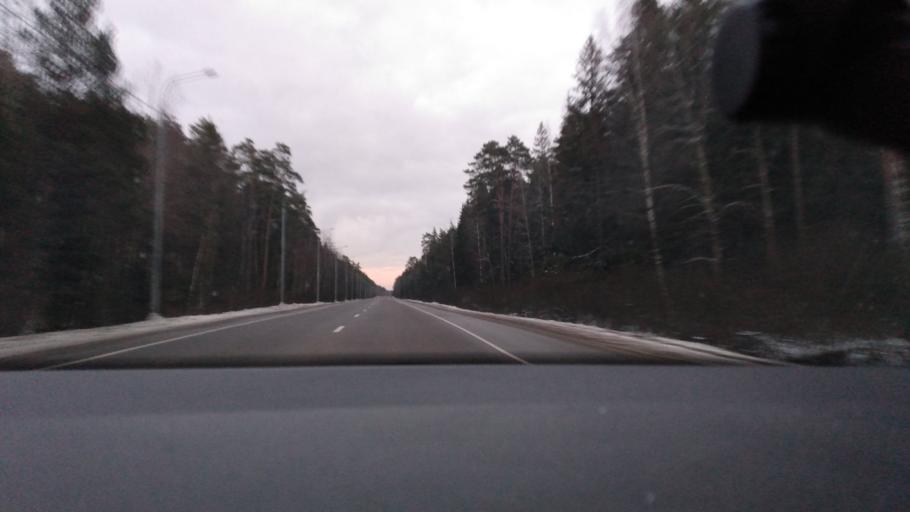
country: RU
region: Moskovskaya
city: Il'inskiy Pogost
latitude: 55.4573
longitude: 38.9902
